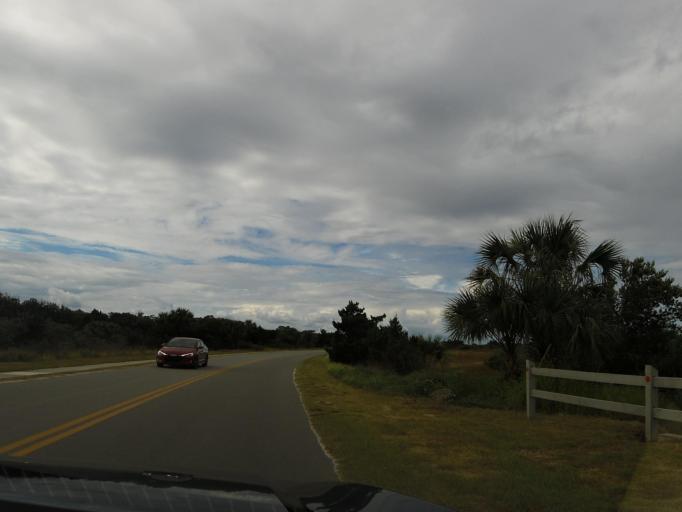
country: US
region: Florida
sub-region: Saint Johns County
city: Saint Augustine Beach
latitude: 29.8669
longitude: -81.2736
